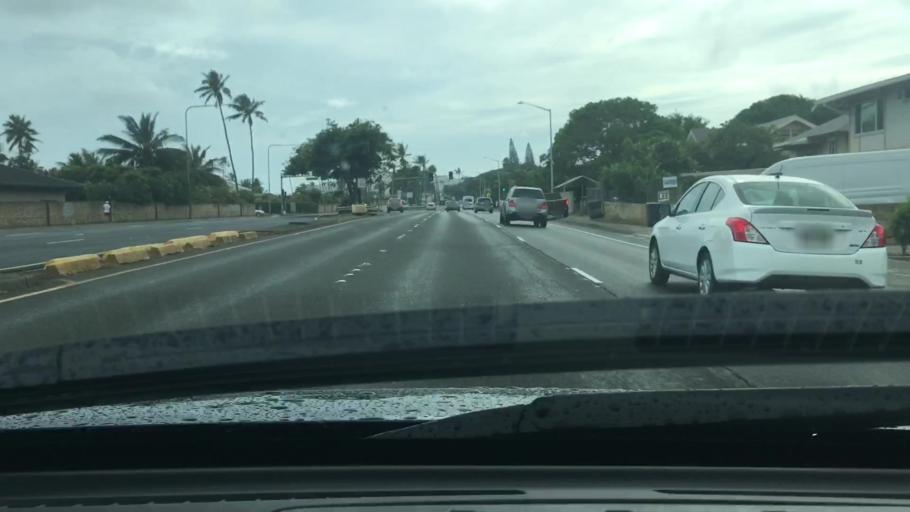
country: US
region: Hawaii
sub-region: Honolulu County
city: Waimanalo
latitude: 21.2777
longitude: -157.7561
